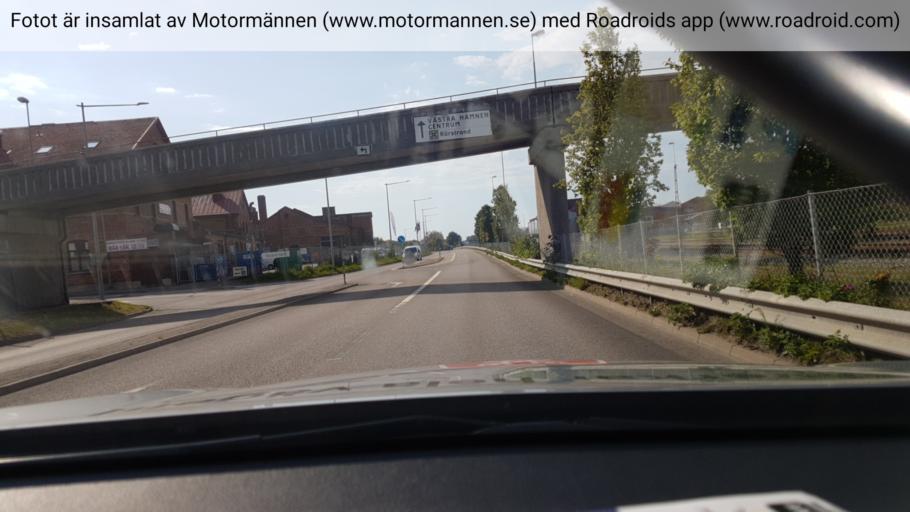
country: SE
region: Vaestra Goetaland
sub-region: Lidkopings Kommun
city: Lidkoping
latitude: 58.5028
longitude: 13.1711
